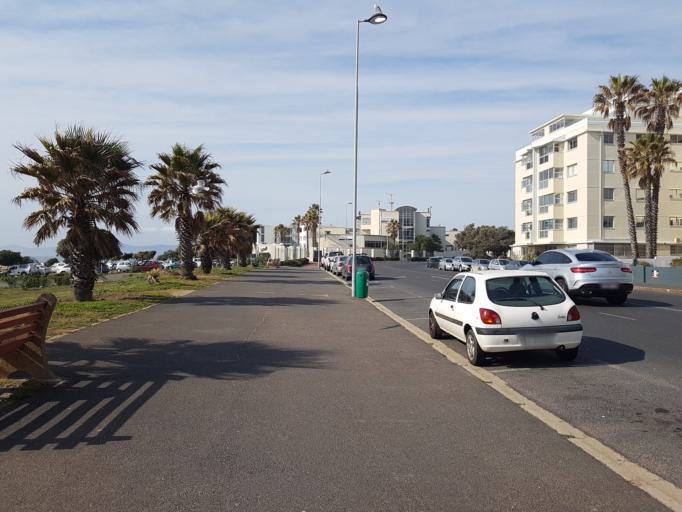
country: ZA
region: Western Cape
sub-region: City of Cape Town
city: Cape Town
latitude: -33.8995
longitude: 18.4099
